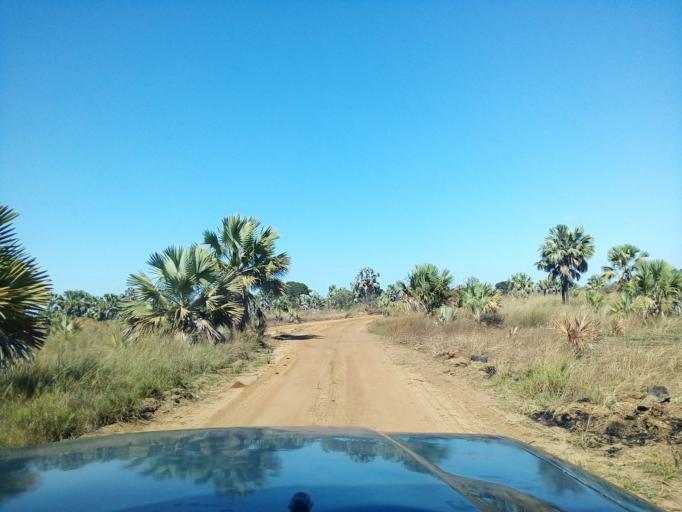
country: MG
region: Boeny
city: Mahajanga
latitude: -15.8551
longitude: 46.1524
